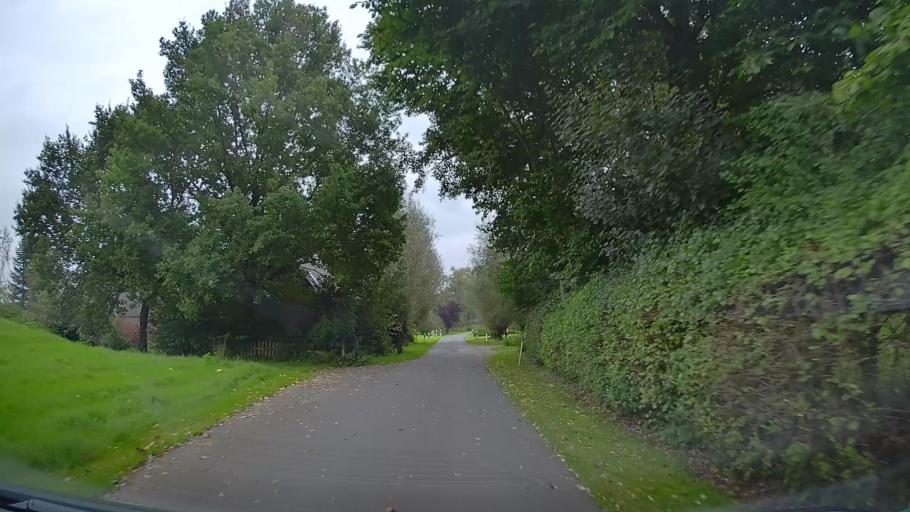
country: DE
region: Lower Saxony
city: Freiburg
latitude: 53.8278
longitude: 9.2610
